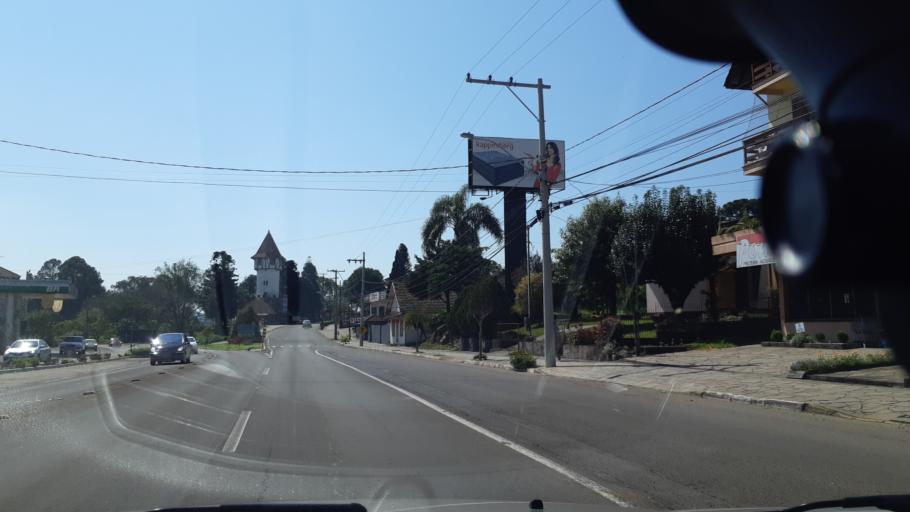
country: BR
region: Rio Grande do Sul
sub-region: Nova Petropolis
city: Nova Petropolis
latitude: -29.3853
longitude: -51.1219
